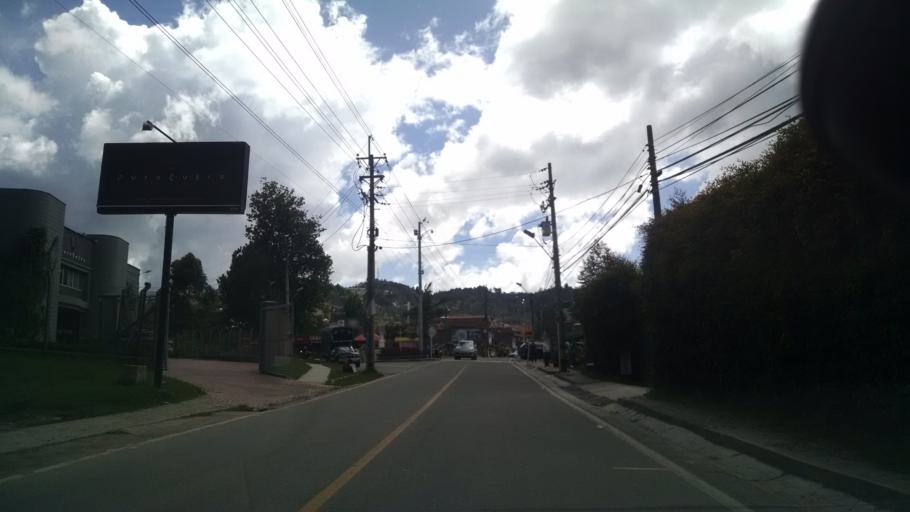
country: CO
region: Antioquia
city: El Retiro
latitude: 6.0654
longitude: -75.5008
